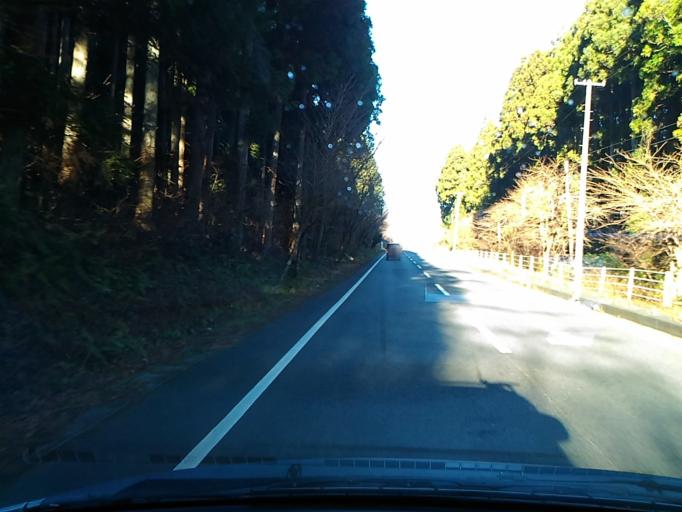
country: JP
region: Ibaraki
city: Kitaibaraki
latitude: 36.9212
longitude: 140.7036
